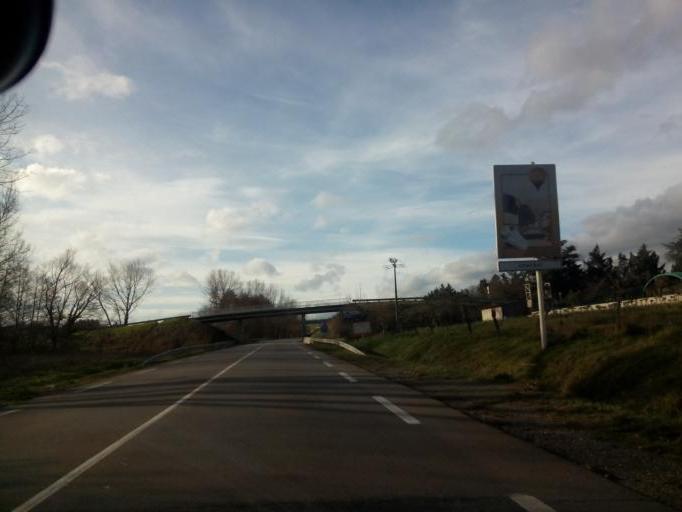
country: FR
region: Rhone-Alpes
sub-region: Departement de l'Ardeche
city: Peaugres
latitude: 45.2870
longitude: 4.7325
